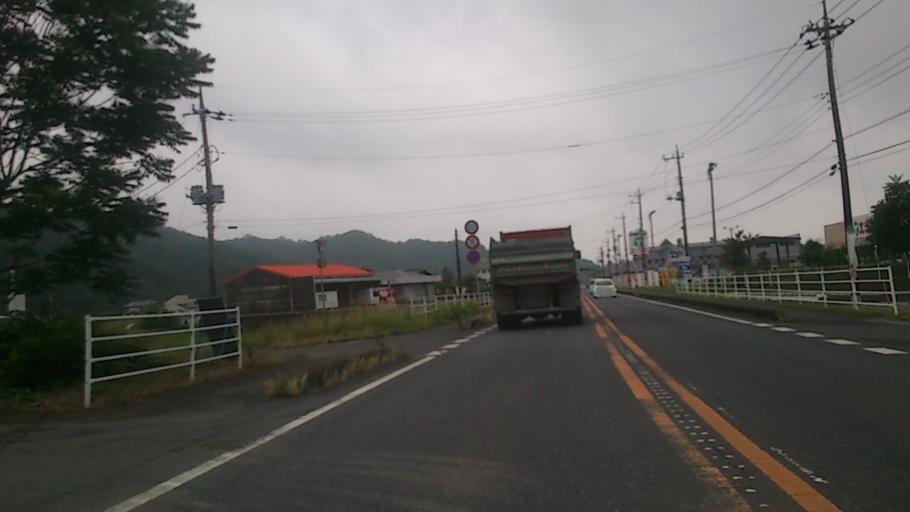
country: JP
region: Ibaraki
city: Omiya
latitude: 36.6301
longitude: 140.4002
